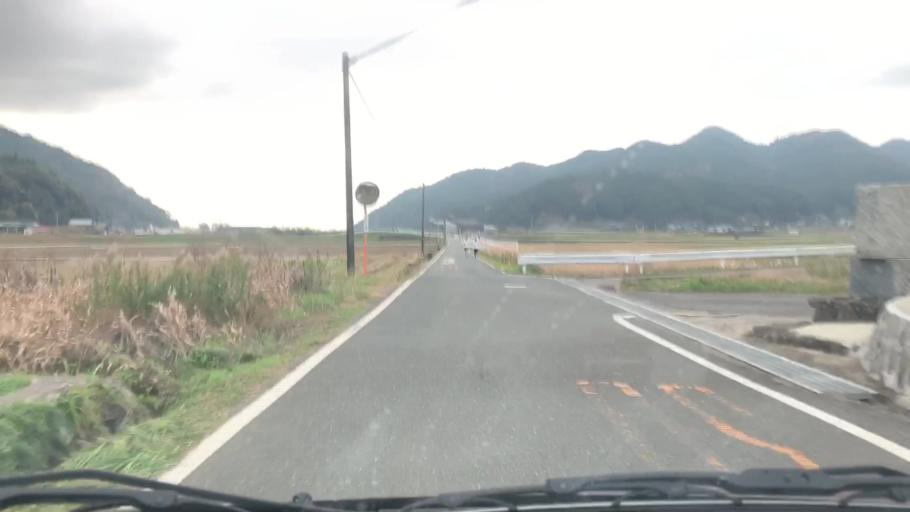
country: JP
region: Saga Prefecture
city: Ureshinomachi-shimojuku
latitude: 33.1271
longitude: 130.0318
